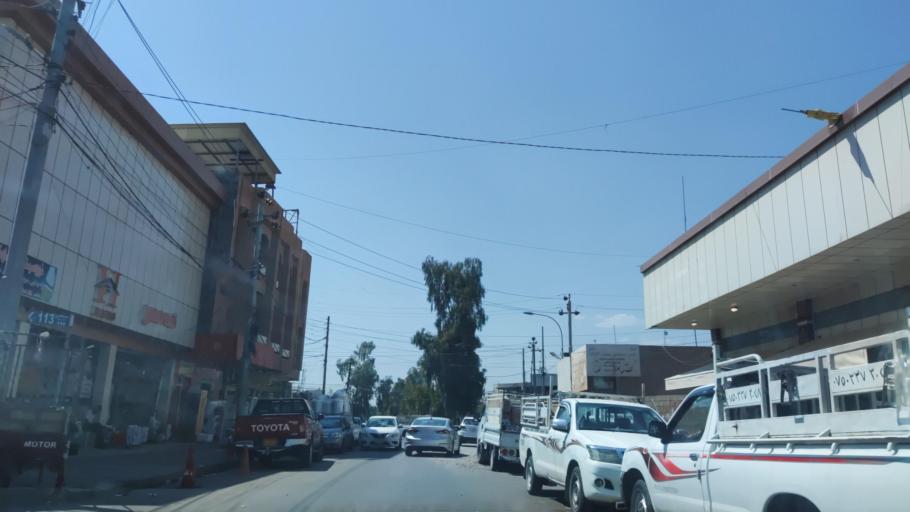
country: IQ
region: Arbil
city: Erbil
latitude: 36.1881
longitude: 44.0199
